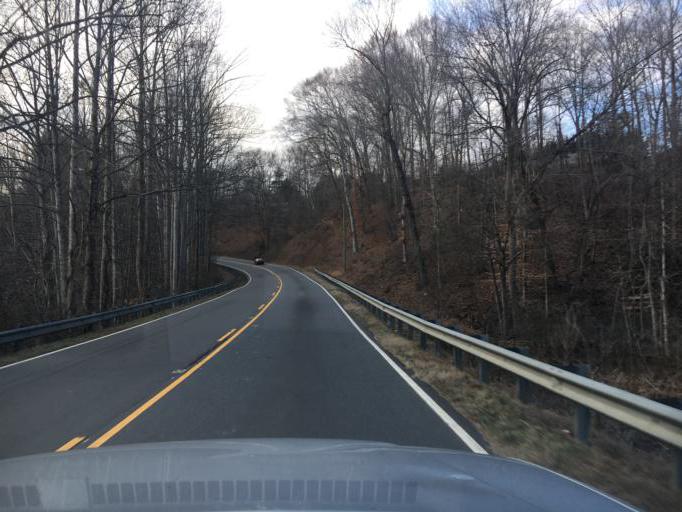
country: US
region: North Carolina
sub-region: Burke County
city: Salem
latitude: 35.6990
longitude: -81.7157
